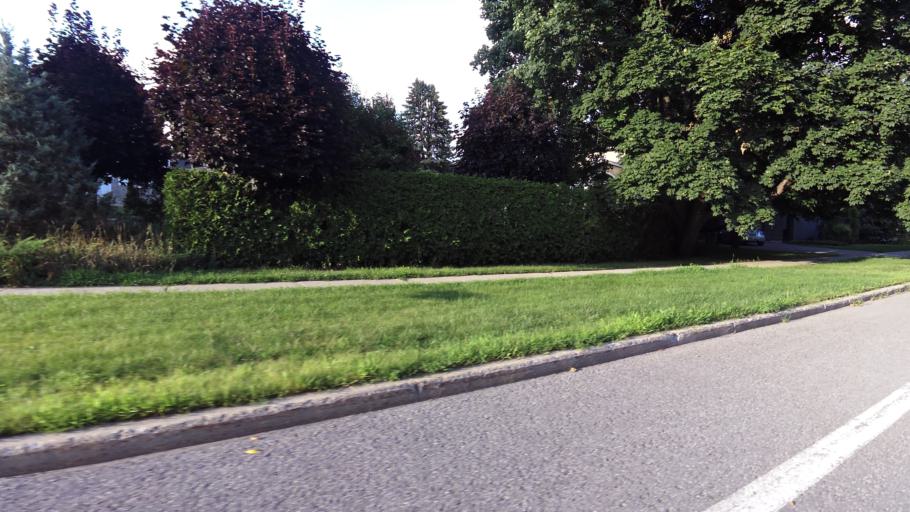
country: CA
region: Ontario
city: Ottawa
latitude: 45.3969
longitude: -75.7196
